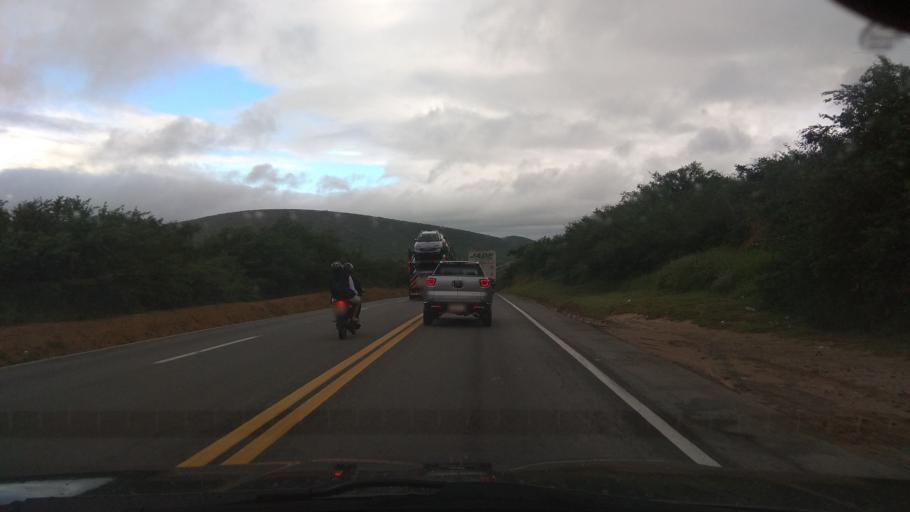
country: BR
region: Bahia
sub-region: Santa Ines
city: Santa Ines
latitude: -13.2567
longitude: -40.0122
